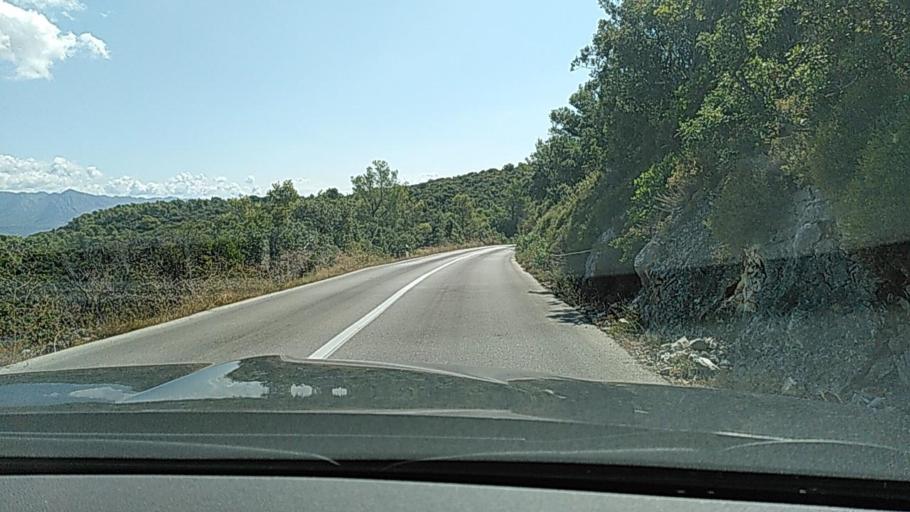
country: HR
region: Dubrovacko-Neretvanska
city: Orebic
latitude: 43.1317
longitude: 17.1327
